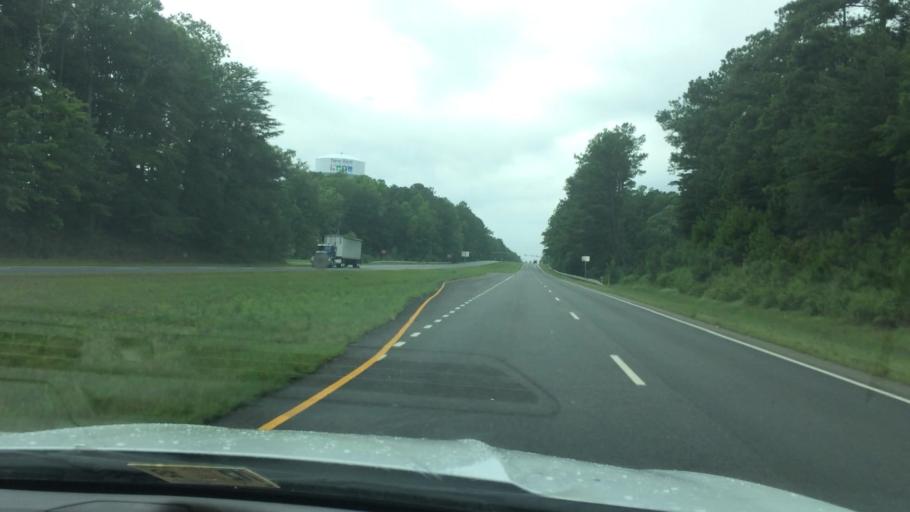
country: US
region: Virginia
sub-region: King William County
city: West Point
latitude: 37.5035
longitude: -76.8677
